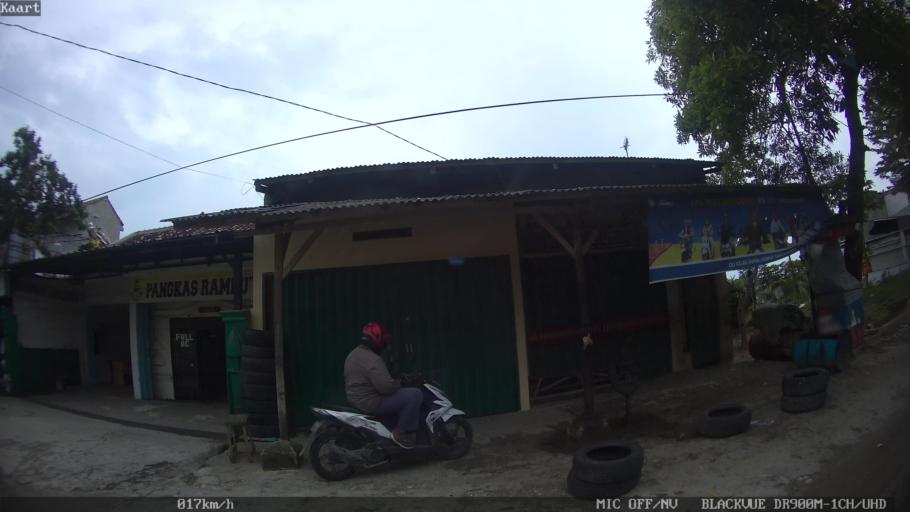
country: ID
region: Lampung
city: Kedaton
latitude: -5.3747
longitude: 105.2144
